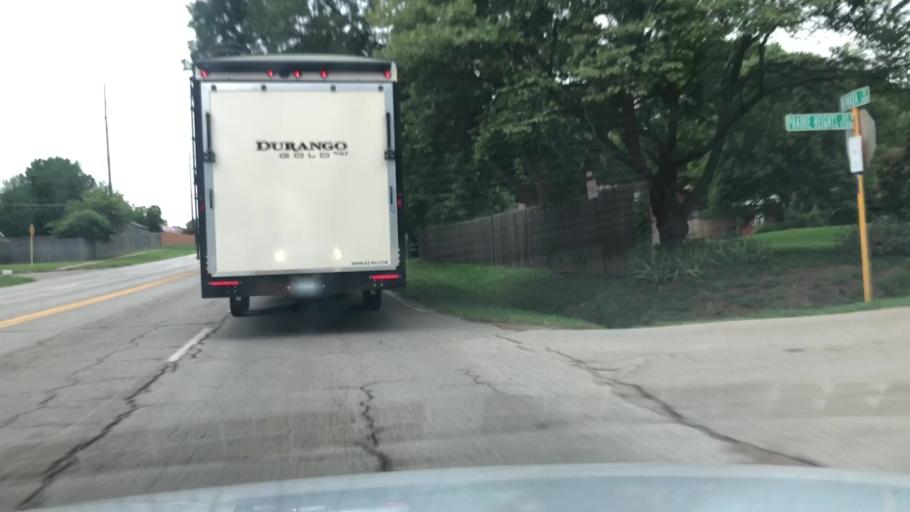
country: US
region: Oklahoma
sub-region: Washington County
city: Bartlesville
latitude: 36.7281
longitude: -95.9155
